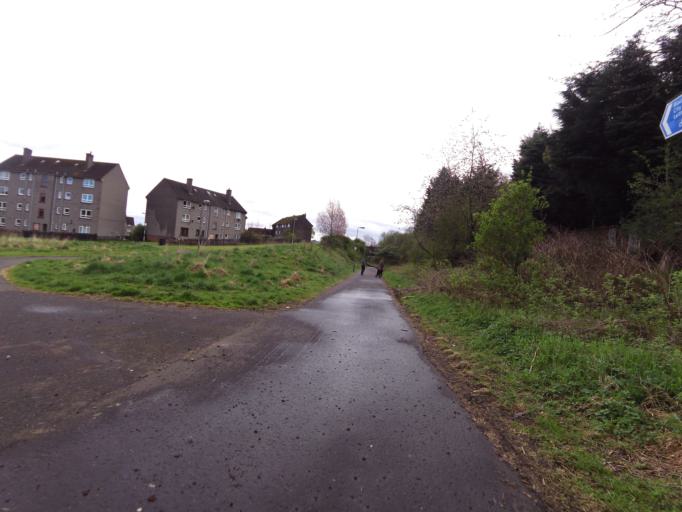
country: GB
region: Scotland
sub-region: Edinburgh
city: Colinton
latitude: 55.9613
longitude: -3.2509
